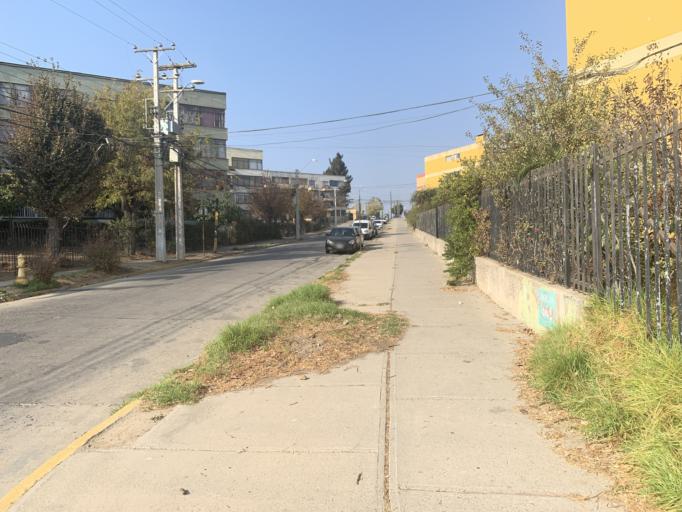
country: CL
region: Valparaiso
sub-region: Provincia de Marga Marga
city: Quilpue
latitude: -33.0495
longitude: -71.4344
